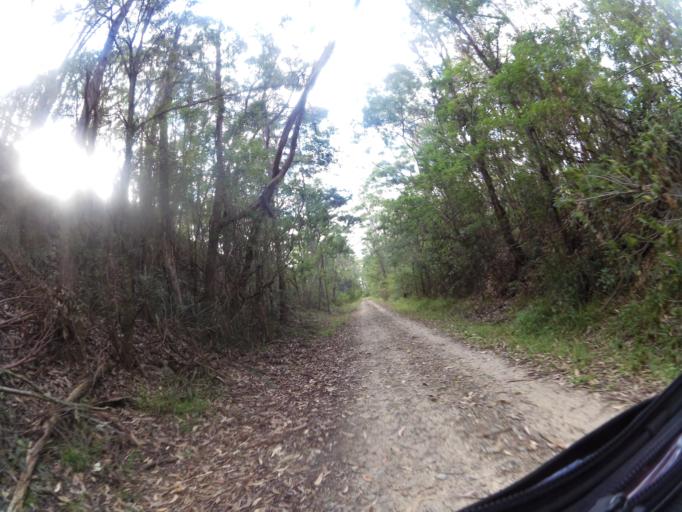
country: AU
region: Victoria
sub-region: East Gippsland
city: Lakes Entrance
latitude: -37.7305
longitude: 148.4260
